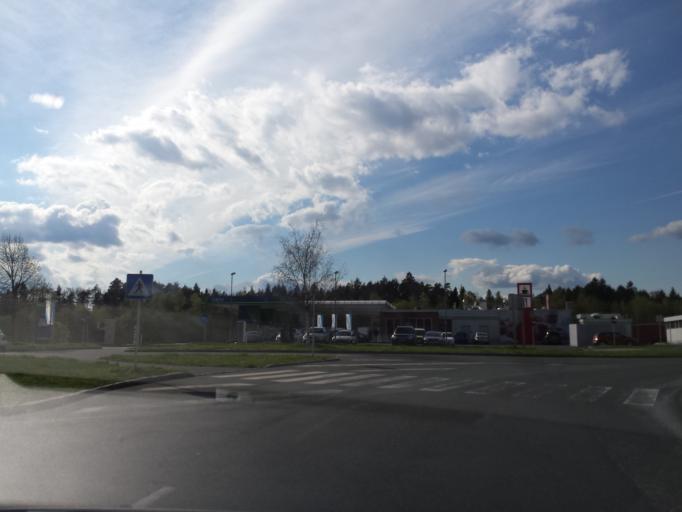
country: AT
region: Styria
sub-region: Politischer Bezirk Graz-Umgebung
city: Unterpremstatten
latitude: 46.9591
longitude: 15.3826
